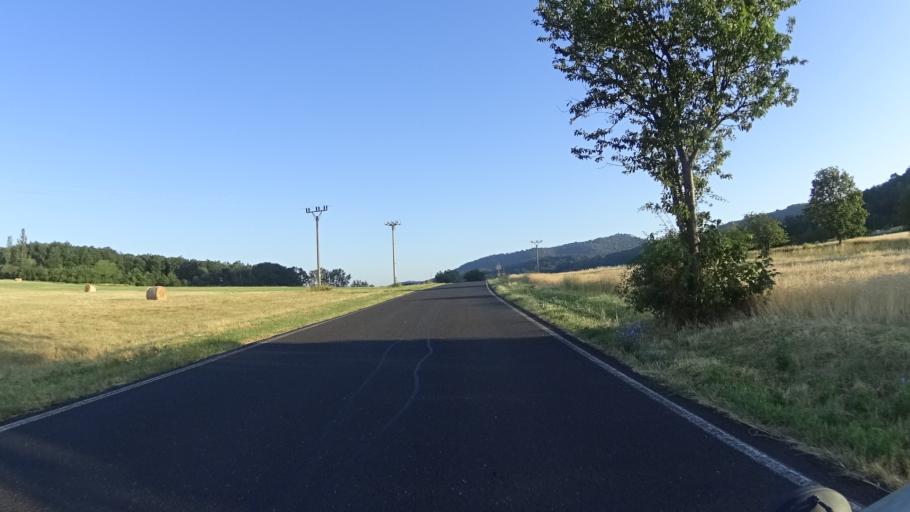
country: CZ
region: Ustecky
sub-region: Okres Litomerice
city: Litomerice
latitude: 50.5651
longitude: 14.1082
